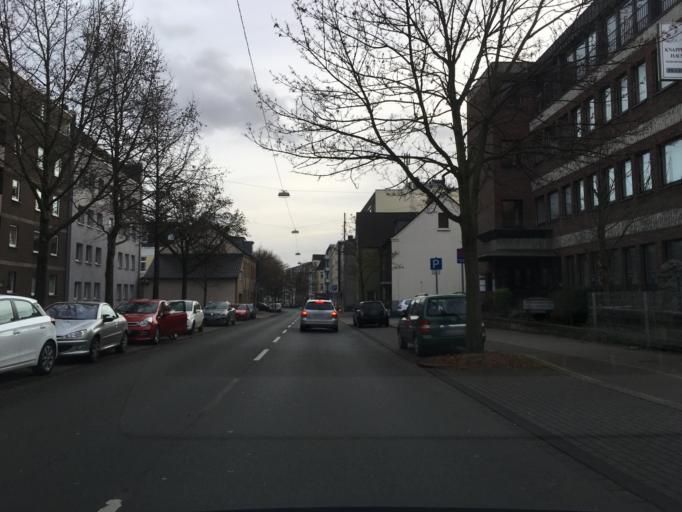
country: DE
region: North Rhine-Westphalia
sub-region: Regierungsbezirk Dusseldorf
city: Oberhausen
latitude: 51.5114
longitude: 6.8511
